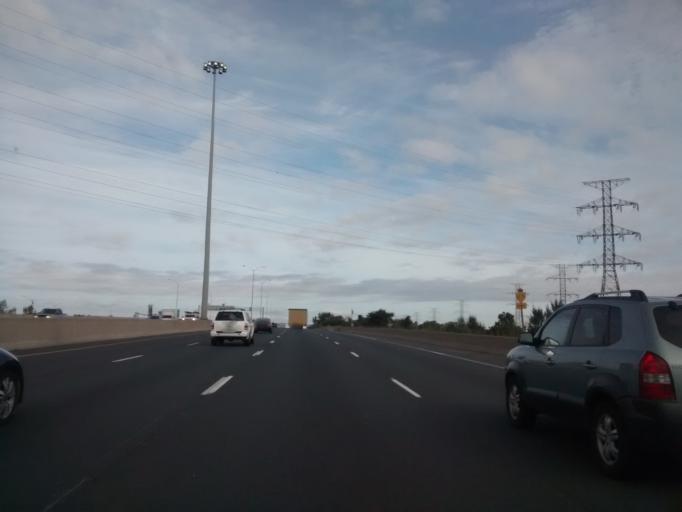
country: CA
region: Ontario
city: Hamilton
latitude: 43.2624
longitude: -79.7708
